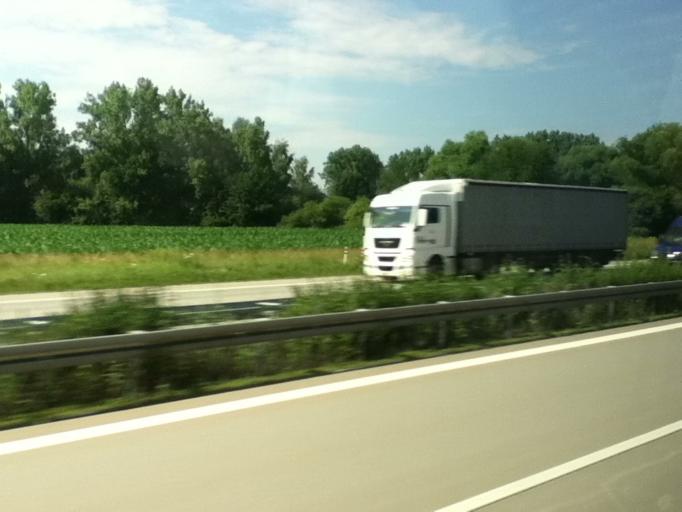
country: DE
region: Saxony
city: Glauchau
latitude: 50.8431
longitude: 12.5388
